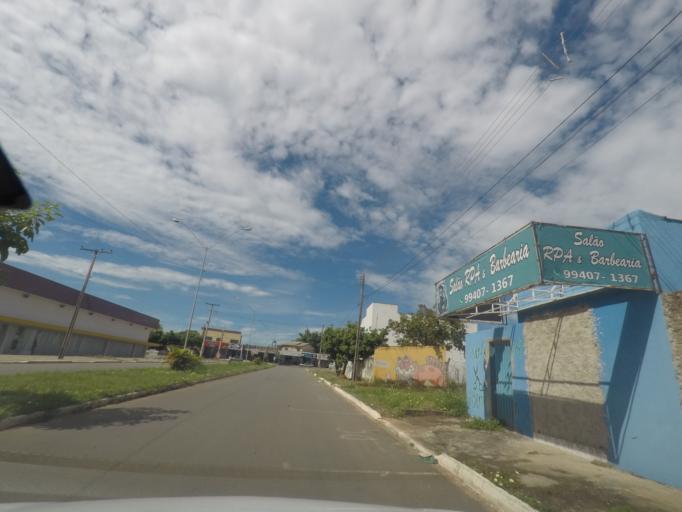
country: BR
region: Goias
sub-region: Aparecida De Goiania
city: Aparecida de Goiania
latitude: -16.8203
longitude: -49.2917
